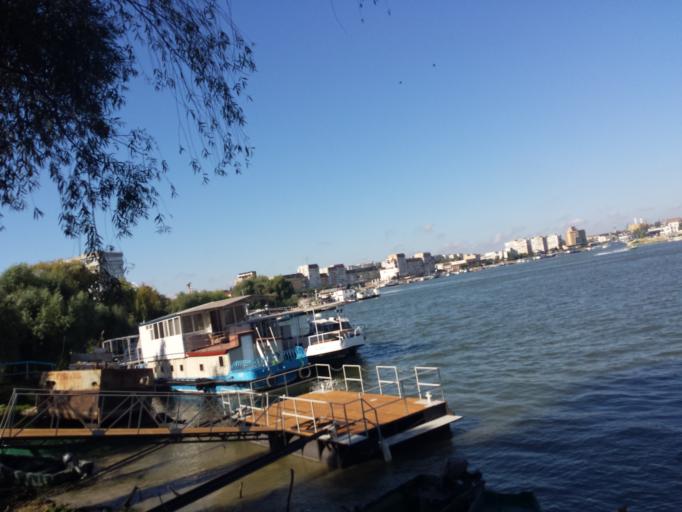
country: RO
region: Tulcea
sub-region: Municipiul Tulcea
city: Tulcea
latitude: 45.1835
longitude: 28.8076
